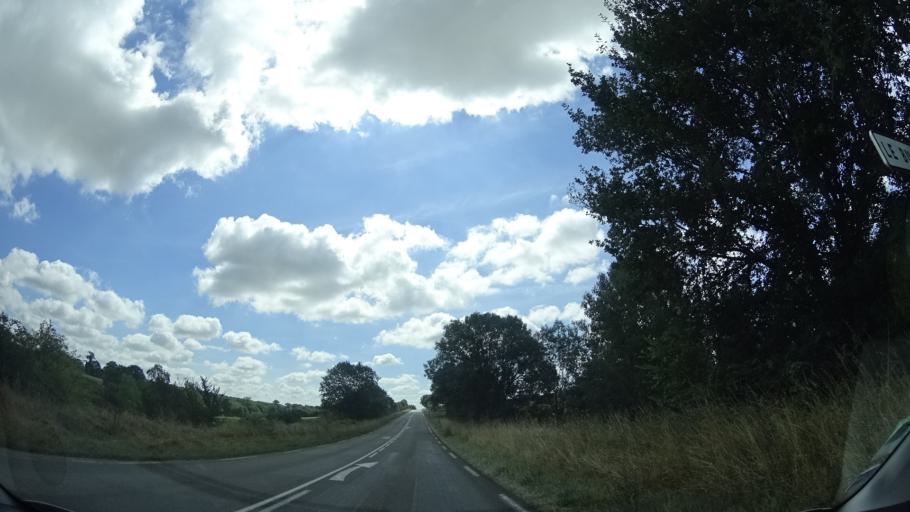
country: FR
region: Pays de la Loire
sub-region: Departement de la Mayenne
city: Meslay-du-Maine
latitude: 47.9382
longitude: -0.5111
